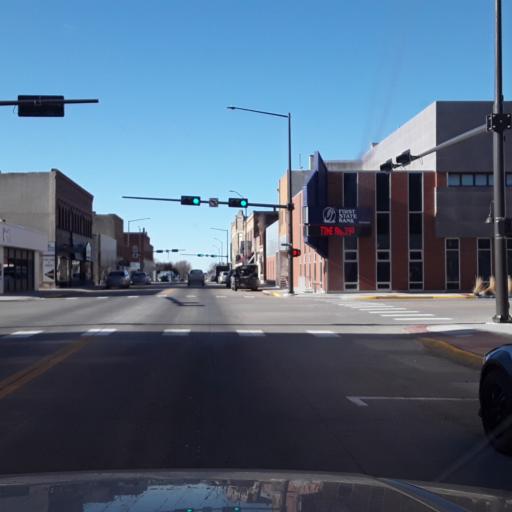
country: US
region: Nebraska
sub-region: Phelps County
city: Holdrege
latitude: 40.4380
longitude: -99.3694
